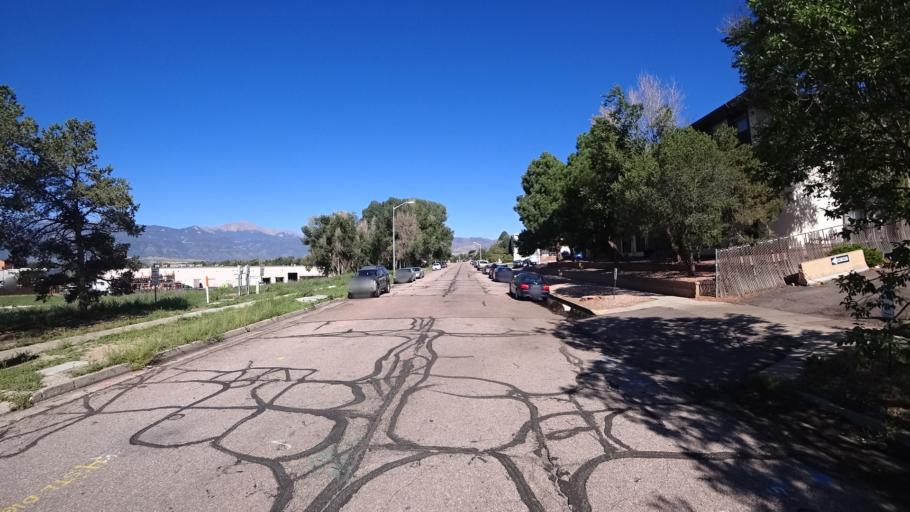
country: US
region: Colorado
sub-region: El Paso County
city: Colorado Springs
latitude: 38.8591
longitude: -104.7901
